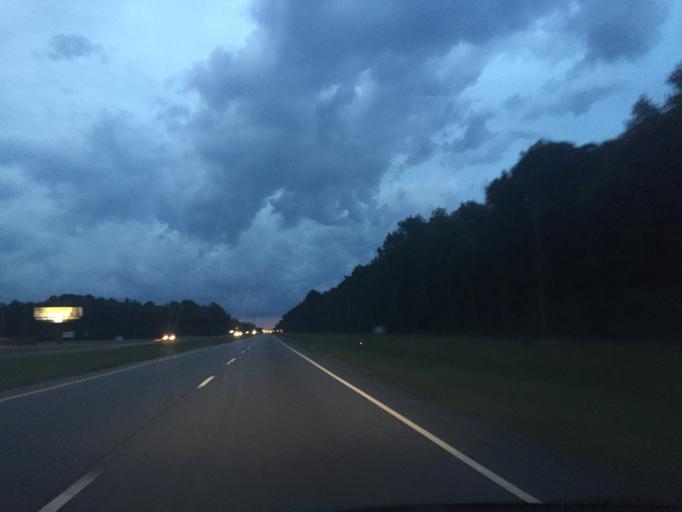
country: US
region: Georgia
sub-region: Bryan County
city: Richmond Hill
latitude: 31.9049
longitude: -81.3625
